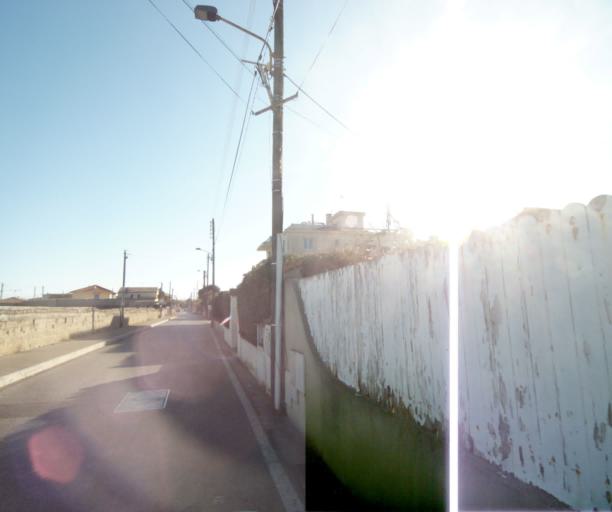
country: FR
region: Provence-Alpes-Cote d'Azur
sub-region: Departement des Alpes-Maritimes
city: Antibes
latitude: 43.5985
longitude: 7.1242
